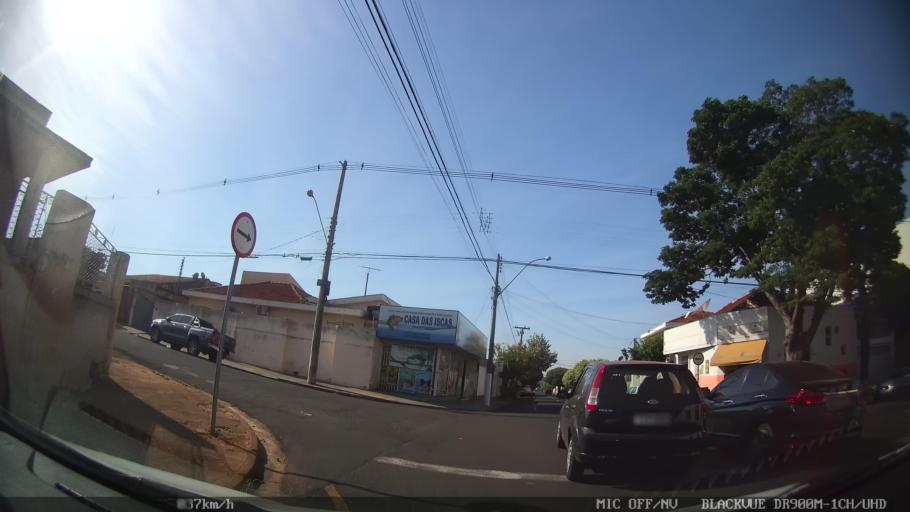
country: BR
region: Sao Paulo
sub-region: Sao Jose Do Rio Preto
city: Sao Jose do Rio Preto
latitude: -20.8008
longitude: -49.3835
